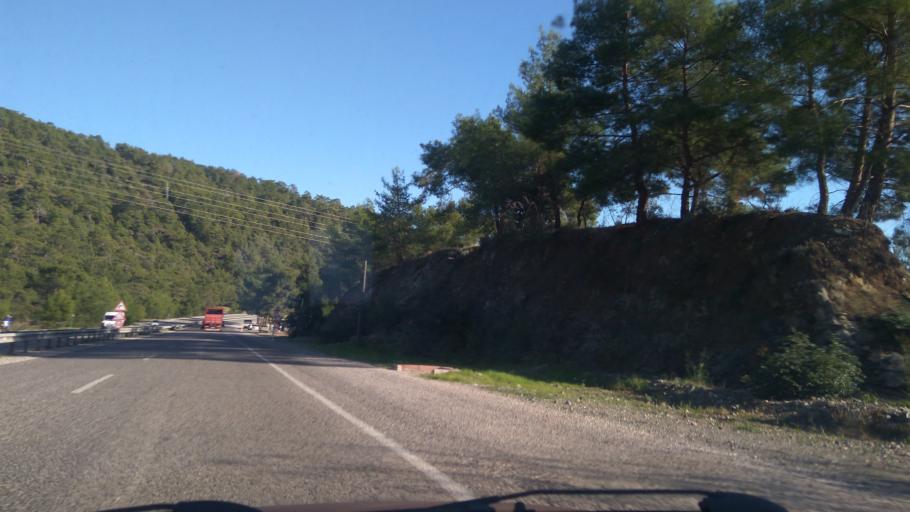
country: TR
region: Antalya
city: Kemer
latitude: 36.5823
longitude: 30.5498
